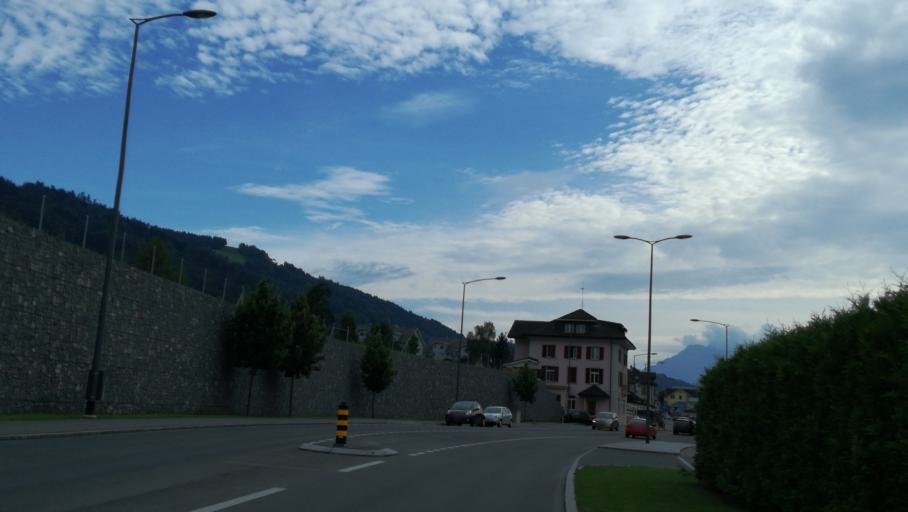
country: CH
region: Lucerne
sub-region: Lucerne-Land District
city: Root
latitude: 47.1220
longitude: 8.3956
